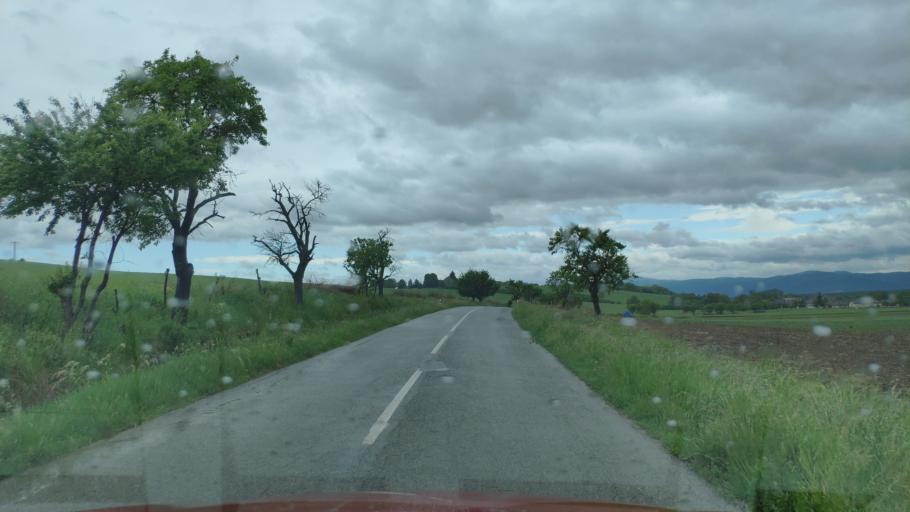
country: SK
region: Kosicky
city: Moldava nad Bodvou
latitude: 48.5384
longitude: 21.0542
